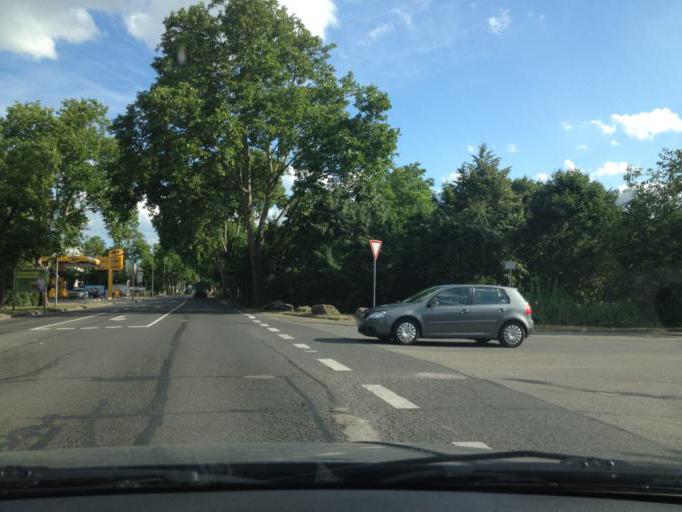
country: DE
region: Rheinland-Pfalz
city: Frankenthal
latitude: 49.5225
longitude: 8.3546
